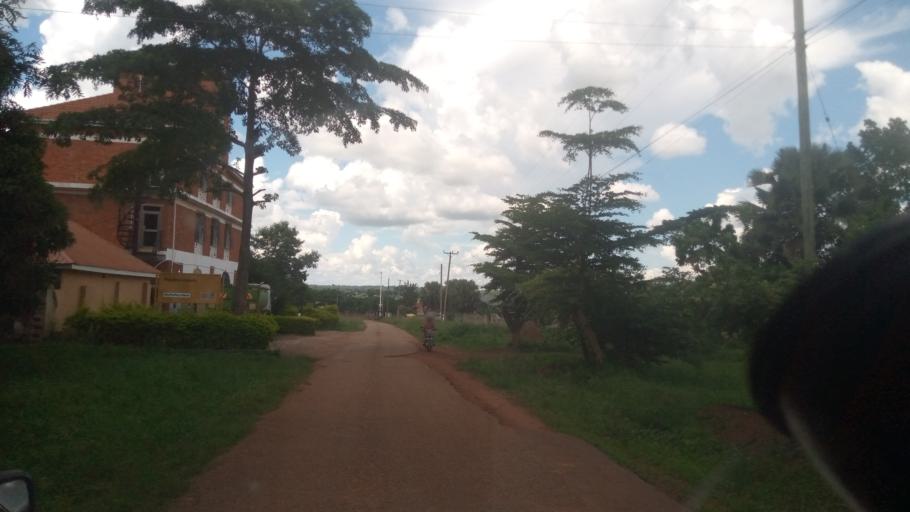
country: UG
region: Northern Region
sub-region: Lira District
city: Lira
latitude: 2.2405
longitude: 32.9071
